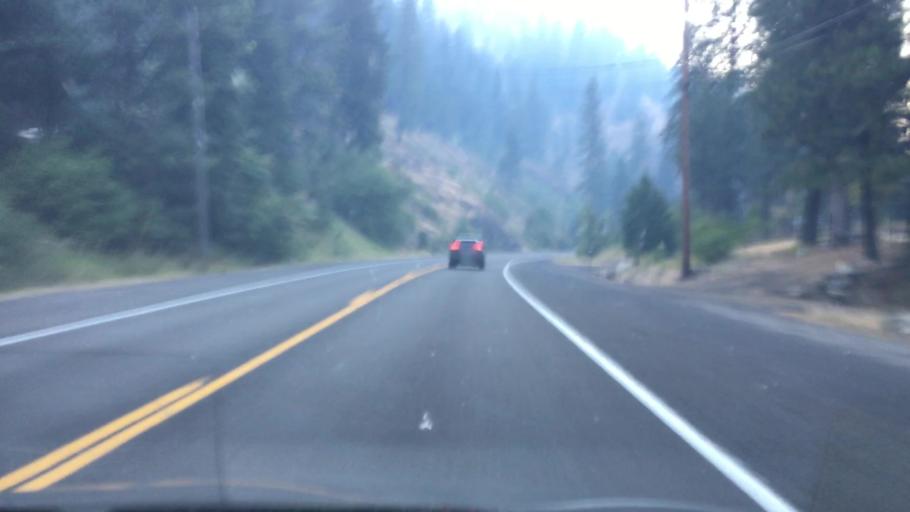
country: US
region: Idaho
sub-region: Valley County
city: McCall
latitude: 45.2296
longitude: -116.3246
